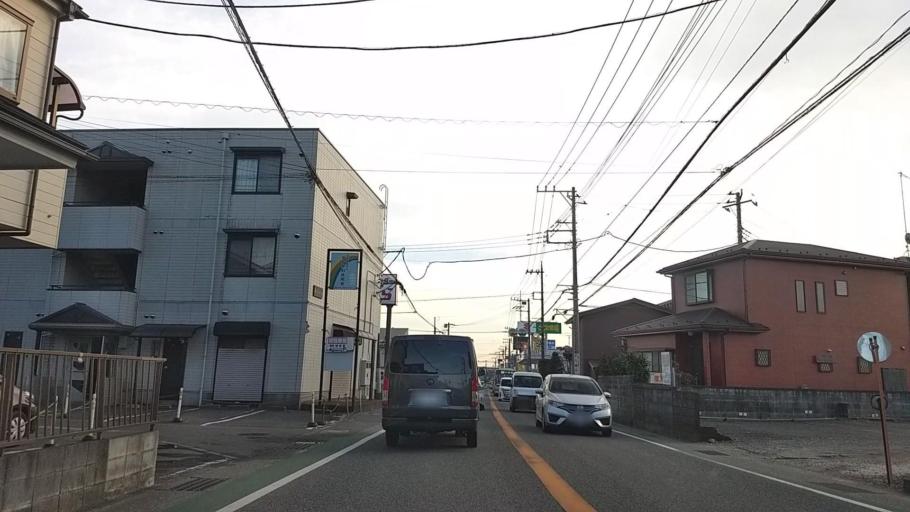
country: JP
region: Kanagawa
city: Atsugi
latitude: 35.4770
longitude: 139.3432
